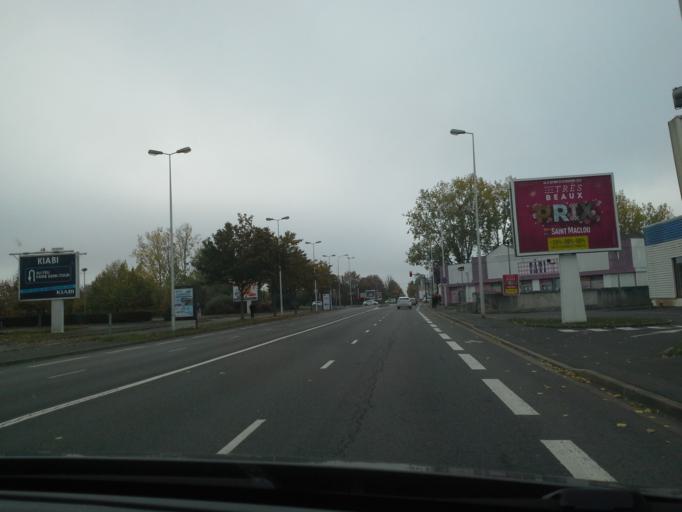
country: FR
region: Centre
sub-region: Departement d'Indre-et-Loire
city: Saint-Cyr-sur-Loire
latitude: 47.4250
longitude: 0.6997
